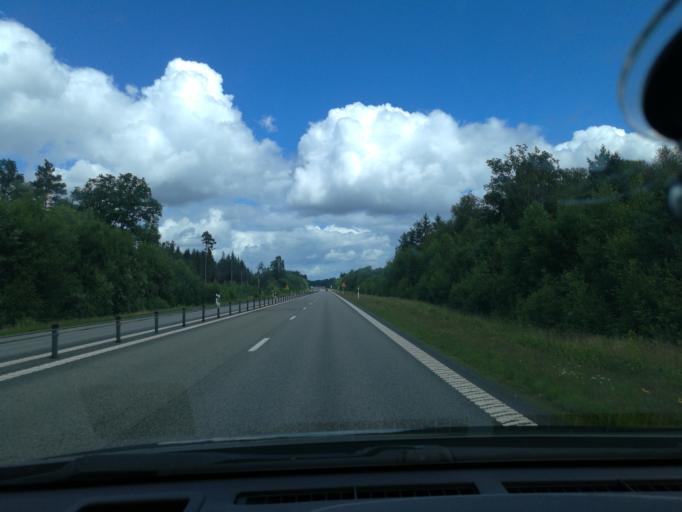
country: SE
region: Skane
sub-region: Hassleholms Kommun
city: Hastveda
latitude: 56.2017
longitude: 13.8596
